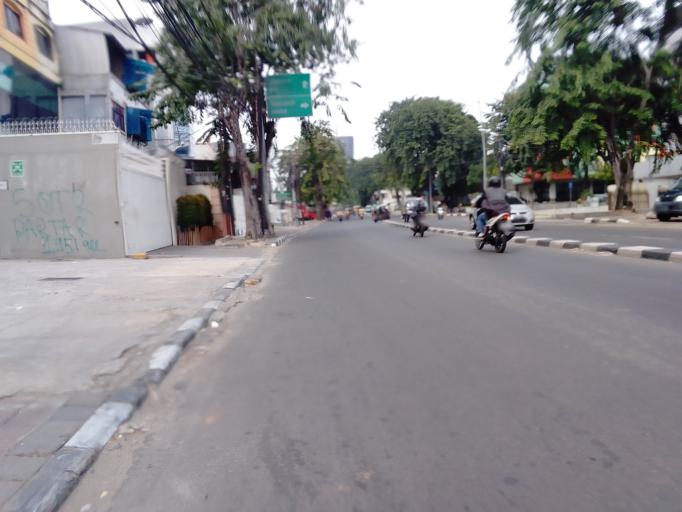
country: ID
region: Jakarta Raya
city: Jakarta
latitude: -6.1607
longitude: 106.8114
